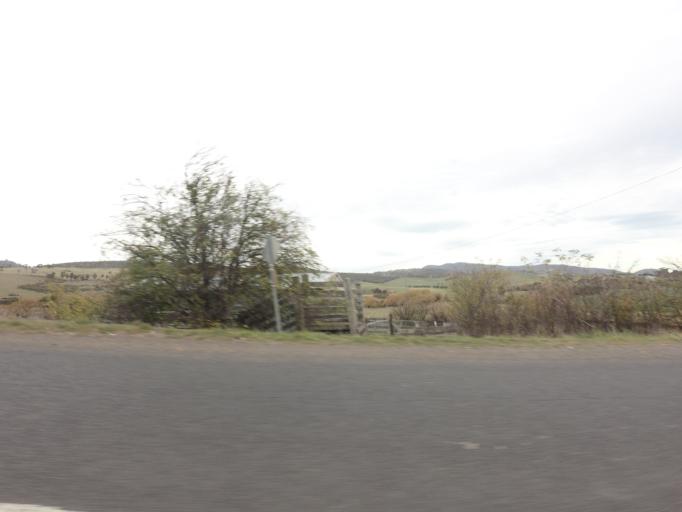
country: AU
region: Tasmania
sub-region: Derwent Valley
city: New Norfolk
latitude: -42.6047
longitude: 147.0771
